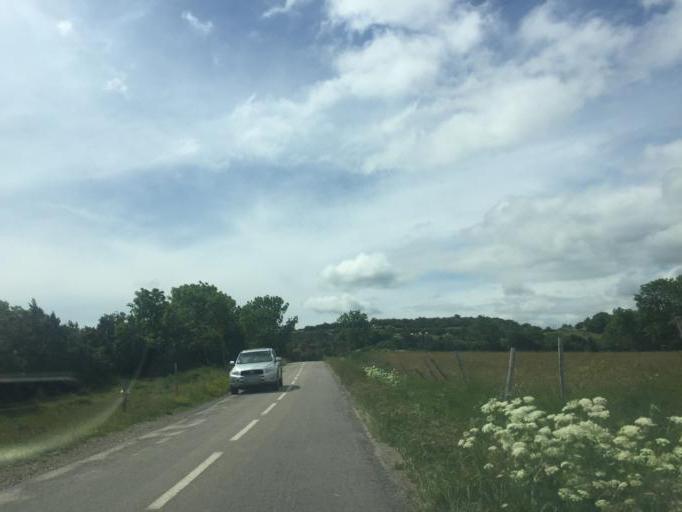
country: FR
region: Rhone-Alpes
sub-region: Departement de l'Ardeche
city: Saint-Priest
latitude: 44.6667
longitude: 4.5636
